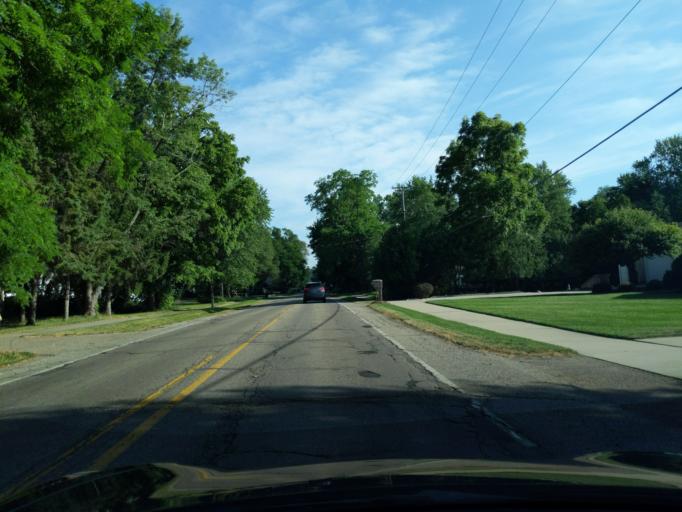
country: US
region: Michigan
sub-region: Ingham County
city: Okemos
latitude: 42.7456
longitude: -84.4277
